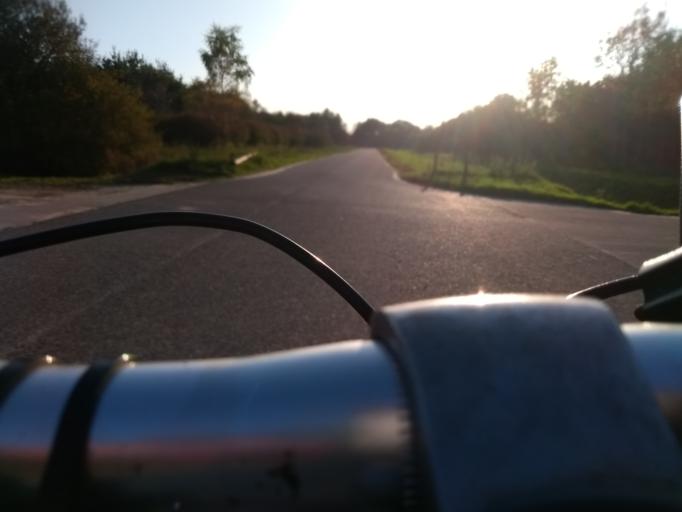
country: NL
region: Drenthe
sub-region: Gemeente Assen
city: Assen
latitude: 52.9564
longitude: 6.5294
